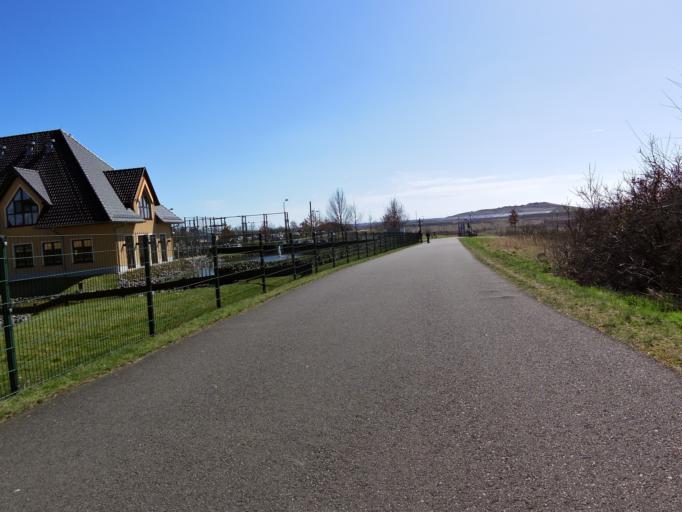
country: DE
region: Saxony
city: Markkleeberg
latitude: 51.2608
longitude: 12.4275
